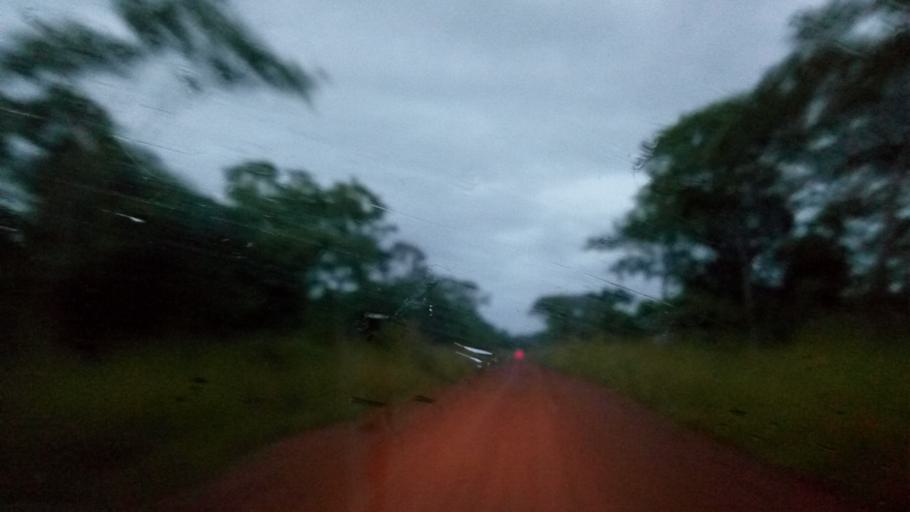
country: ZM
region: Luapula
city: Nchelenge
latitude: -9.8066
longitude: 28.1434
